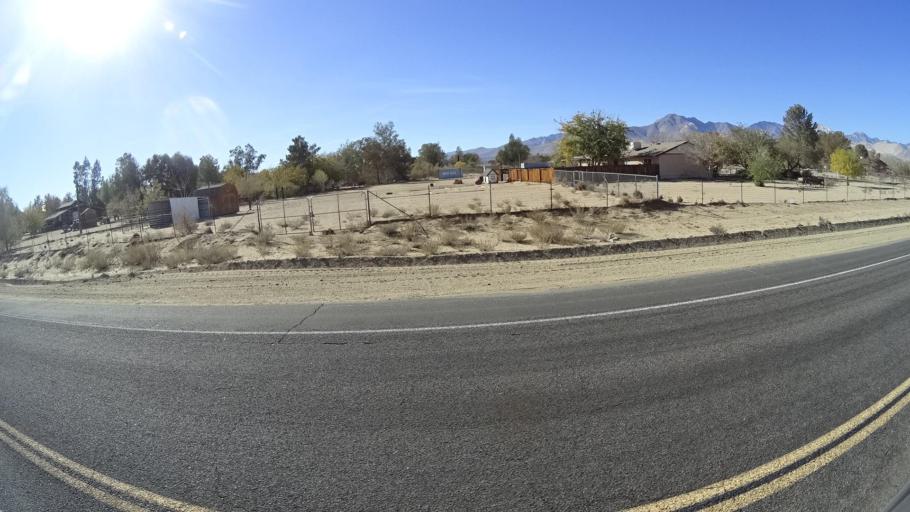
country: US
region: California
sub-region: Kern County
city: Inyokern
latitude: 35.6281
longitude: -117.8068
